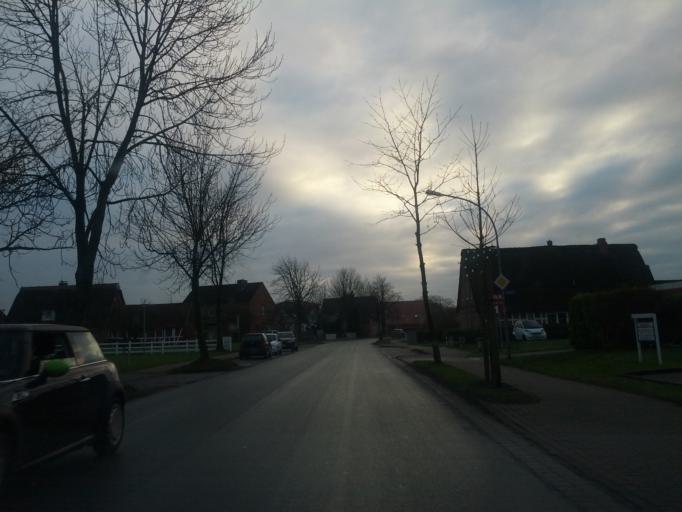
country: DE
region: Lower Saxony
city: Steinkirchen
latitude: 53.5665
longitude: 9.6113
